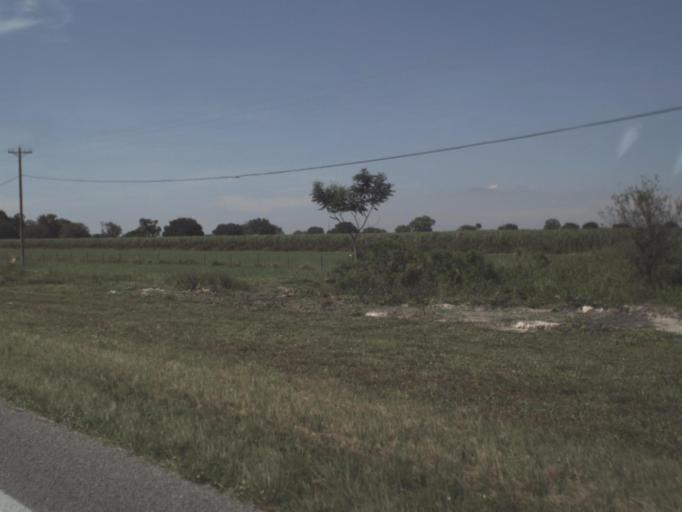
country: US
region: Florida
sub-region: Glades County
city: Moore Haven
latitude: 26.8339
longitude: -81.1469
